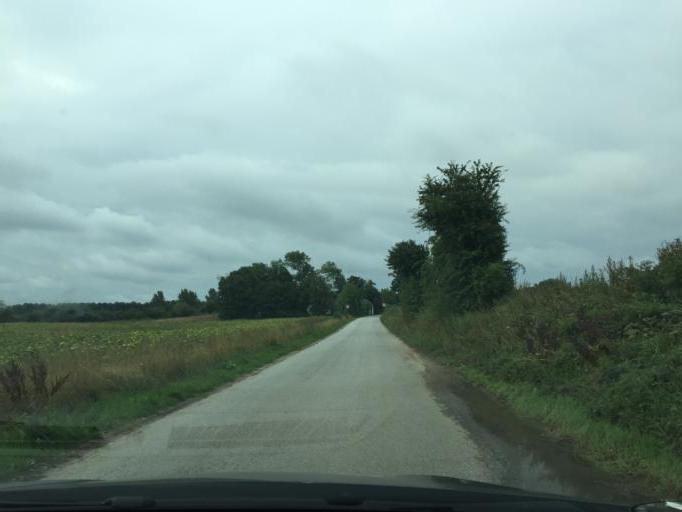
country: DK
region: South Denmark
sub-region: Assens Kommune
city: Harby
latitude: 55.1934
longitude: 10.0834
